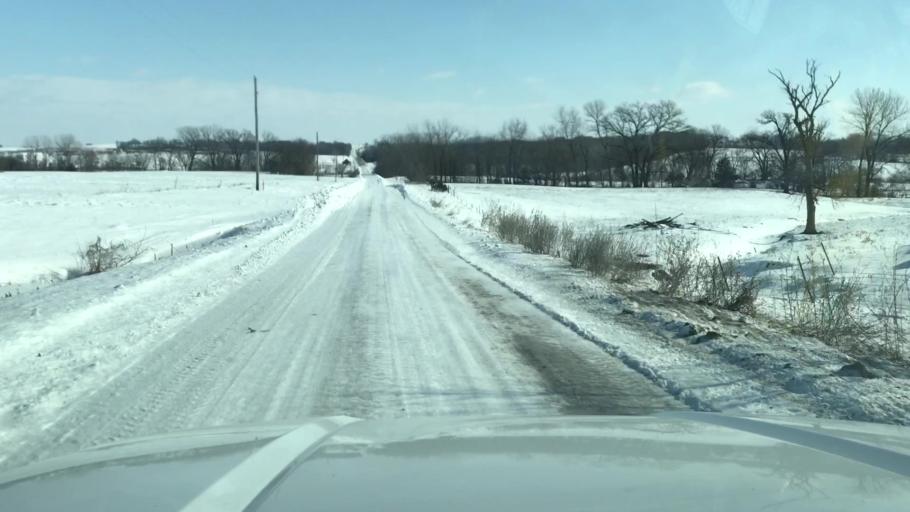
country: US
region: Missouri
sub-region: Nodaway County
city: Maryville
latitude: 40.3865
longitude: -94.6745
